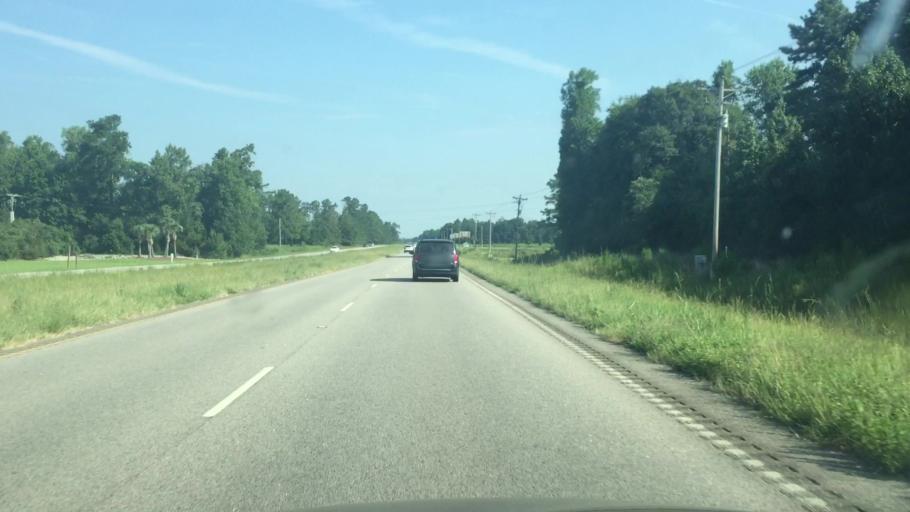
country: US
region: South Carolina
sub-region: Horry County
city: Little River
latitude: 33.9660
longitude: -78.7393
